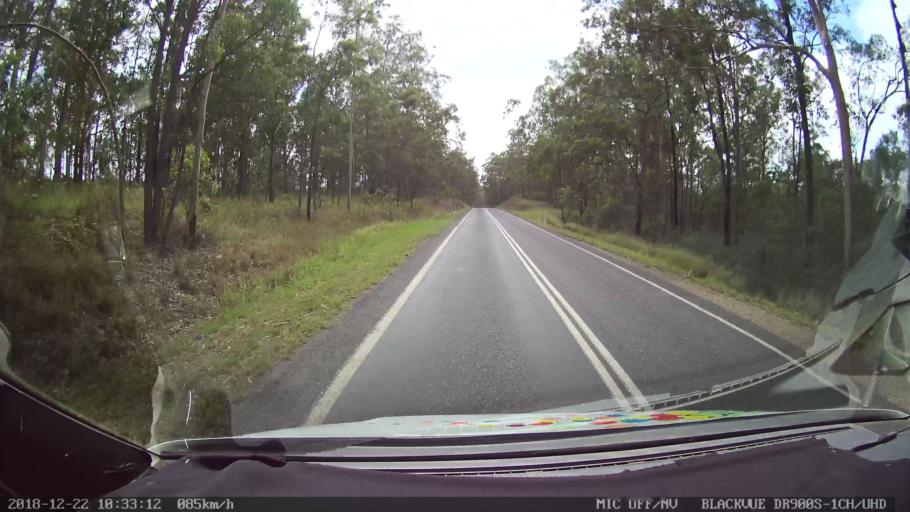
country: AU
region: New South Wales
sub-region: Clarence Valley
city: South Grafton
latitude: -29.6163
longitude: 152.6509
